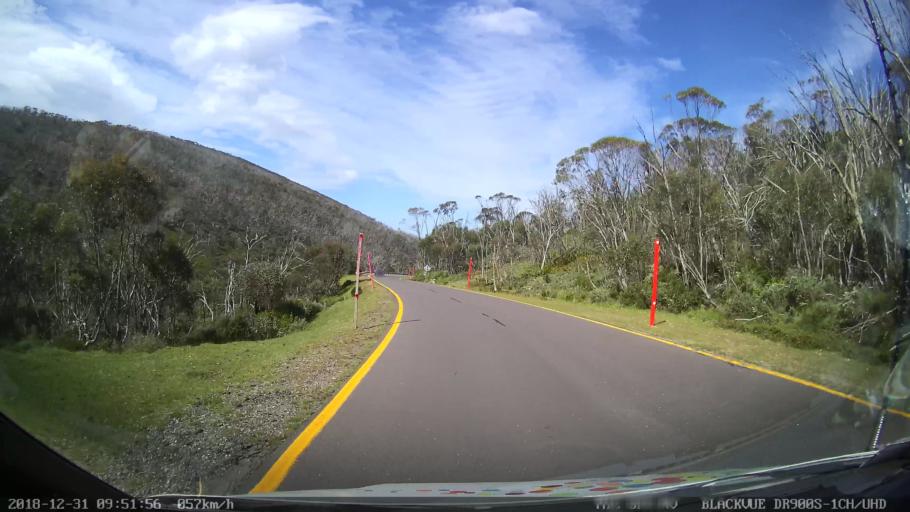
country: AU
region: New South Wales
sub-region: Snowy River
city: Jindabyne
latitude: -36.5247
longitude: 148.2580
